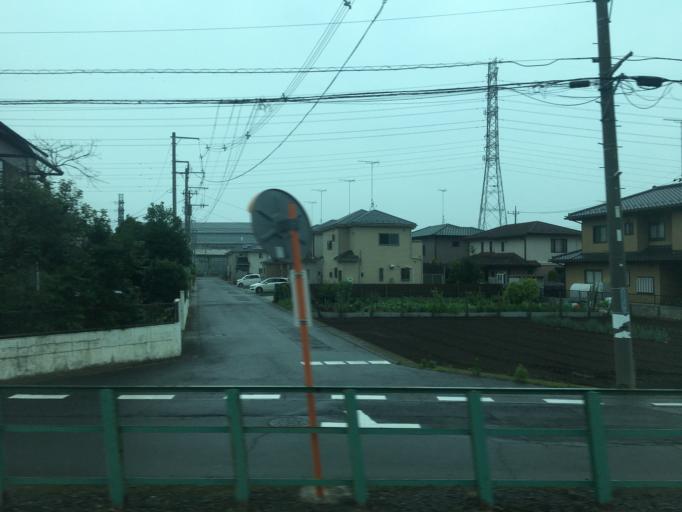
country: JP
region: Tochigi
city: Oyama
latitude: 36.2709
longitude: 139.7722
